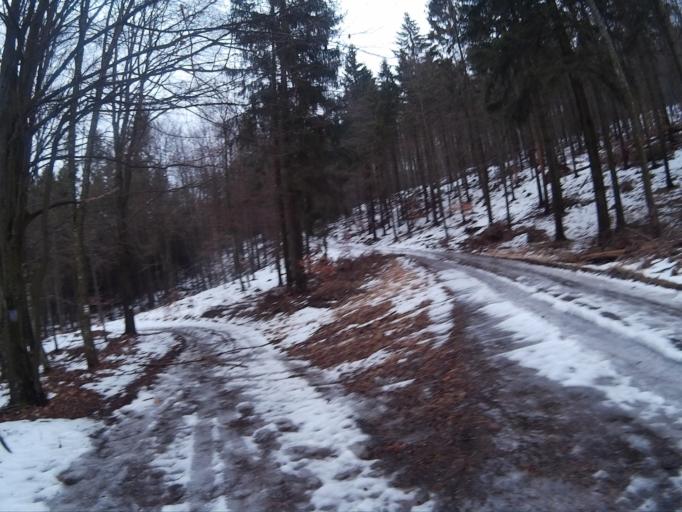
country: HU
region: Heves
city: Belapatfalva
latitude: 48.0515
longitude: 20.3980
